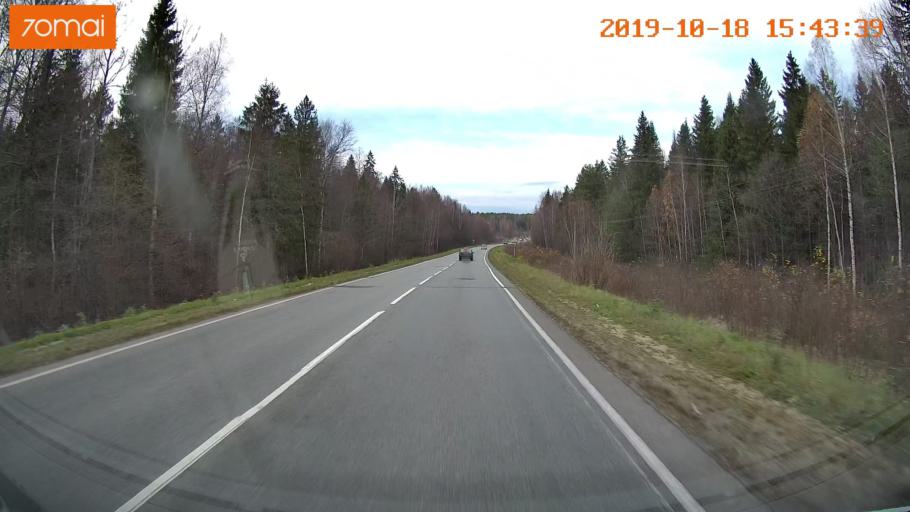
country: RU
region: Vladimir
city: Golovino
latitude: 55.9707
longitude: 40.5488
